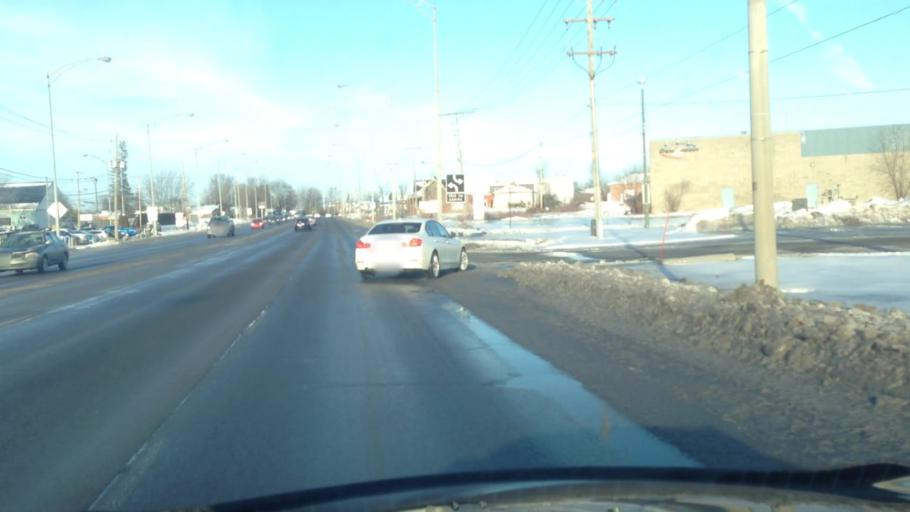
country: CA
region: Quebec
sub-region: Laurentides
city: Saint-Jerome
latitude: 45.7552
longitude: -73.9965
